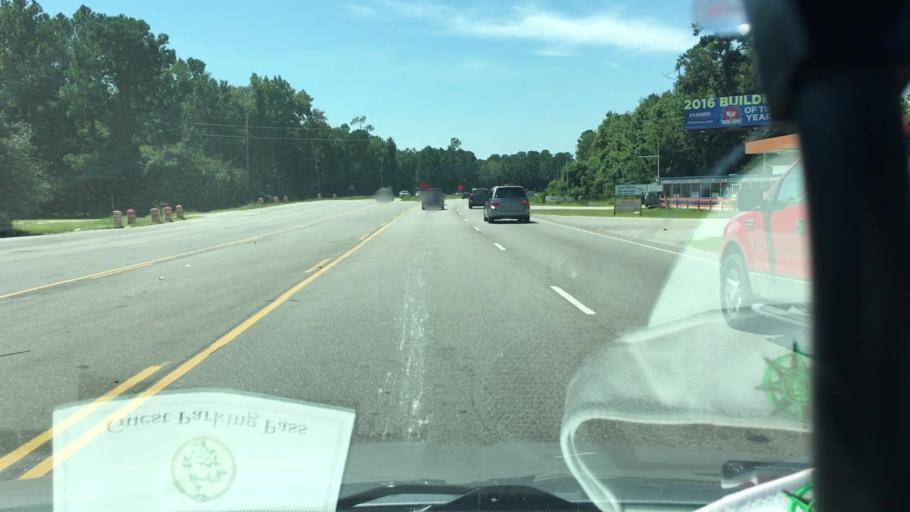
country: US
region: South Carolina
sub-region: Beaufort County
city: Bluffton
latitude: 32.3352
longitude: -80.9283
